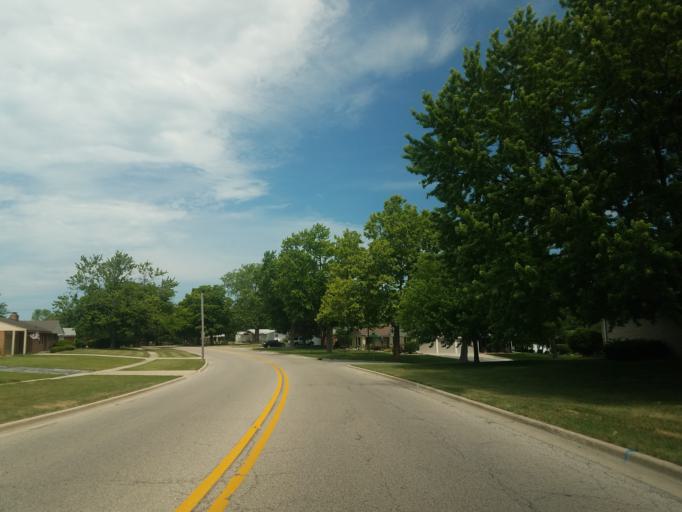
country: US
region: Illinois
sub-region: McLean County
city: Bloomington
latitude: 40.4909
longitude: -88.9613
